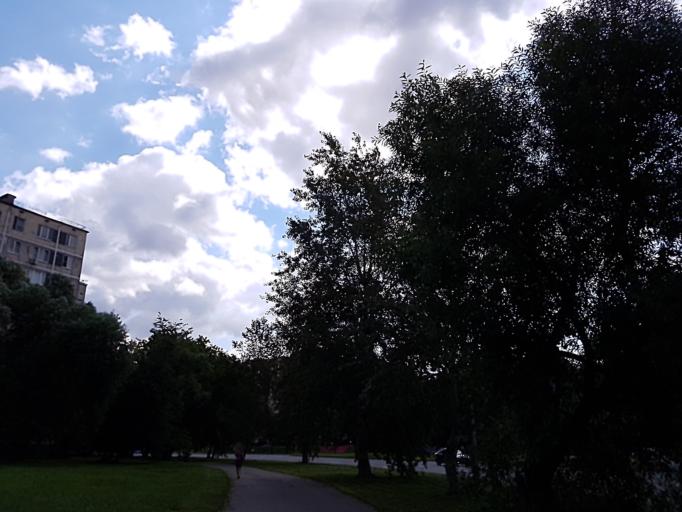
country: RU
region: Moskovskaya
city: Kuskovo
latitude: 55.7392
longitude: 37.8183
